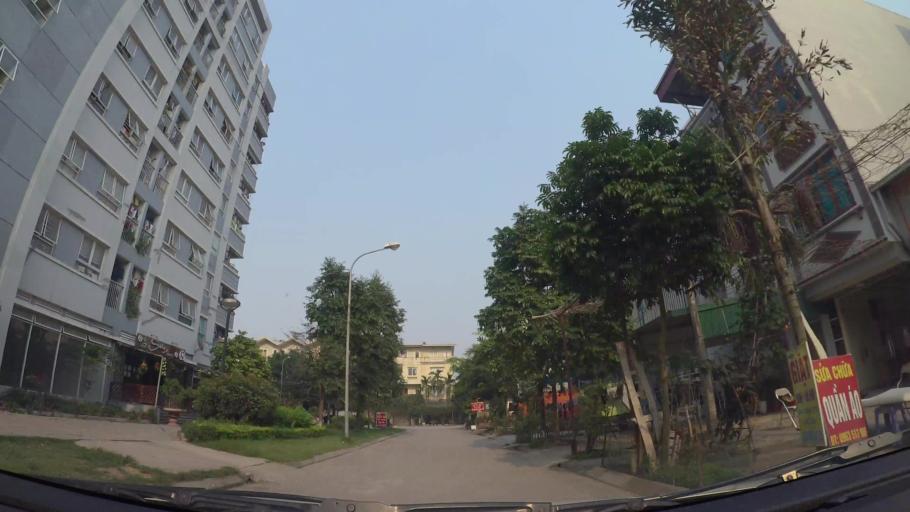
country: VN
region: Ha Noi
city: Ha Dong
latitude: 20.9962
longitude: 105.7473
